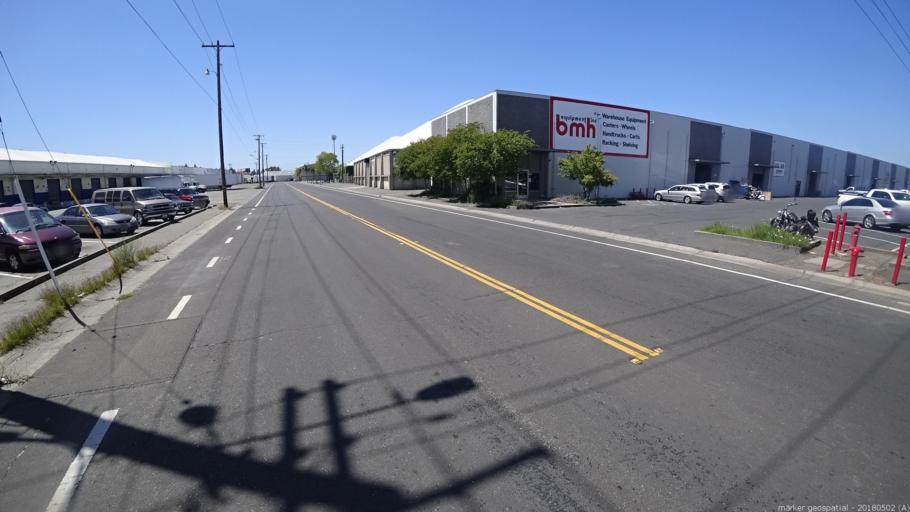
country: US
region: California
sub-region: Sacramento County
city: Sacramento
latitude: 38.6039
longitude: -121.4392
